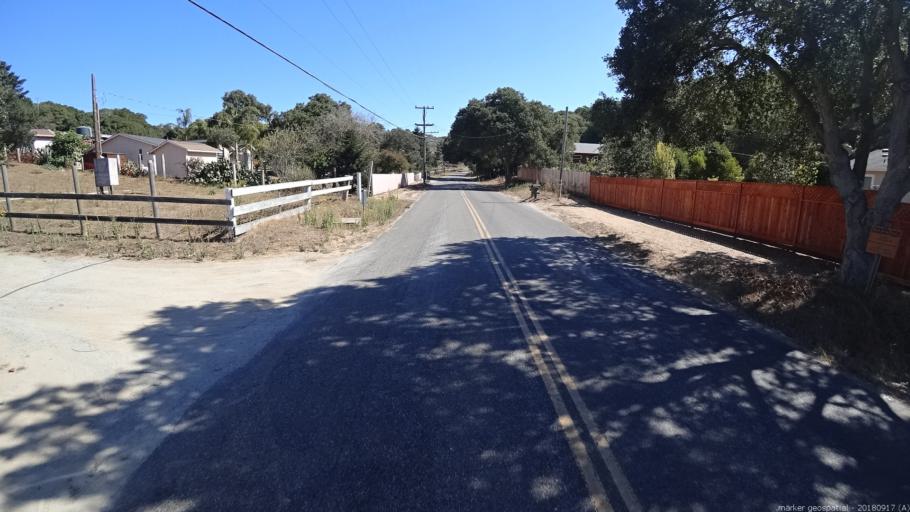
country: US
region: California
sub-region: Monterey County
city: Elkhorn
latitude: 36.8316
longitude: -121.6967
